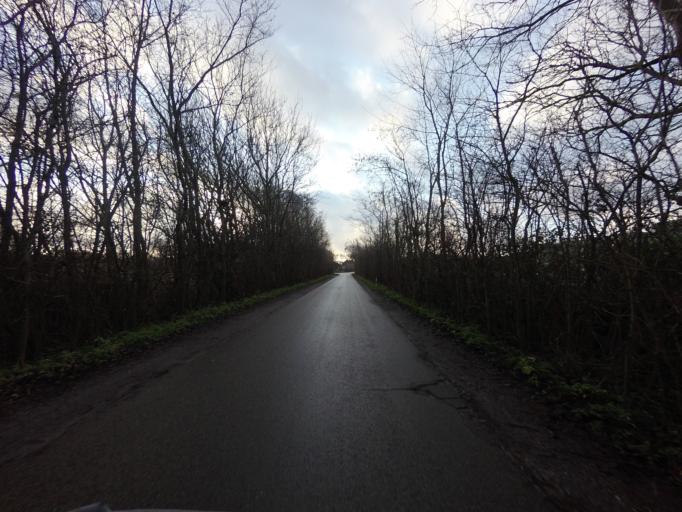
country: NL
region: North Holland
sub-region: Gemeente Texel
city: Den Burg
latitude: 53.0948
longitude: 4.7730
